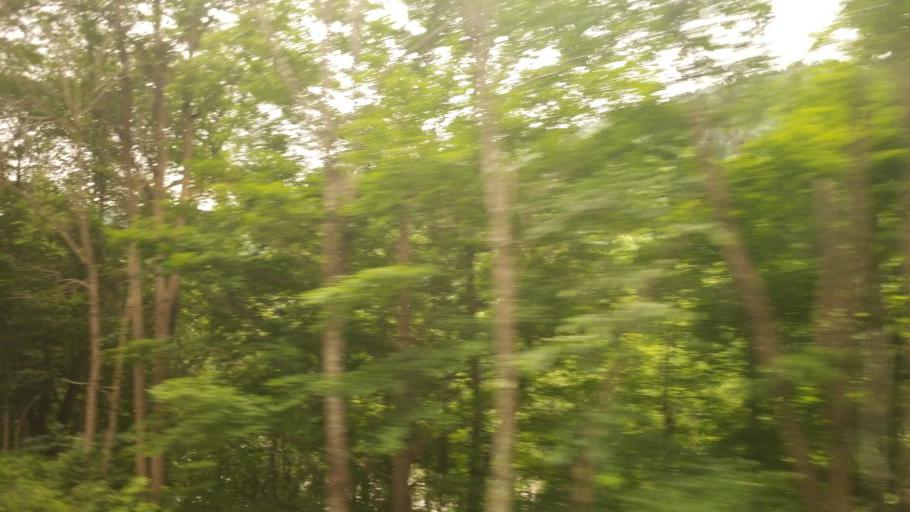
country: US
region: Pennsylvania
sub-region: Fayette County
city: South Connellsville
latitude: 39.9341
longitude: -79.4874
